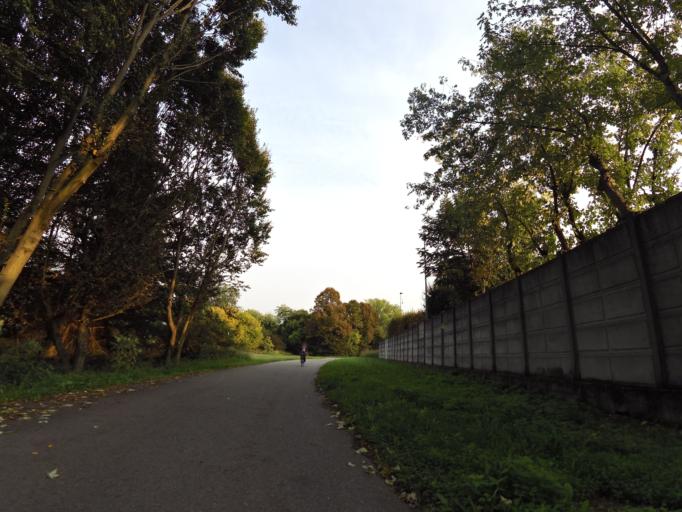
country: IT
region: Lombardy
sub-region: Citta metropolitana di Milano
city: San Donato Milanese
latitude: 45.4192
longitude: 9.2882
